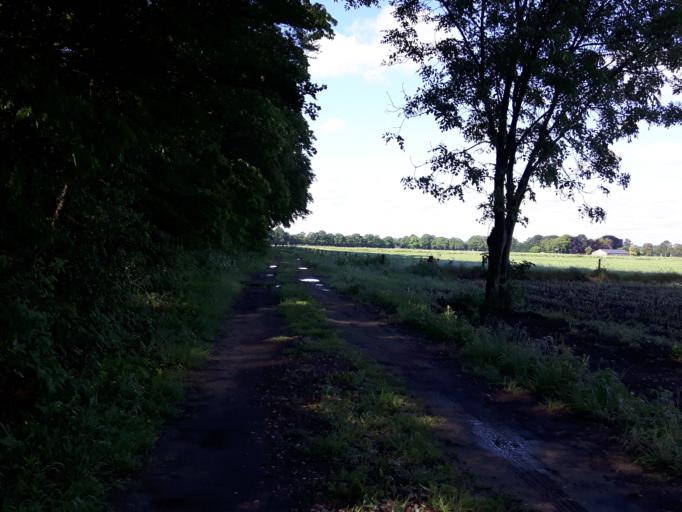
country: NL
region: Overijssel
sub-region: Gemeente Enschede
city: Enschede
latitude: 52.1649
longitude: 6.8564
